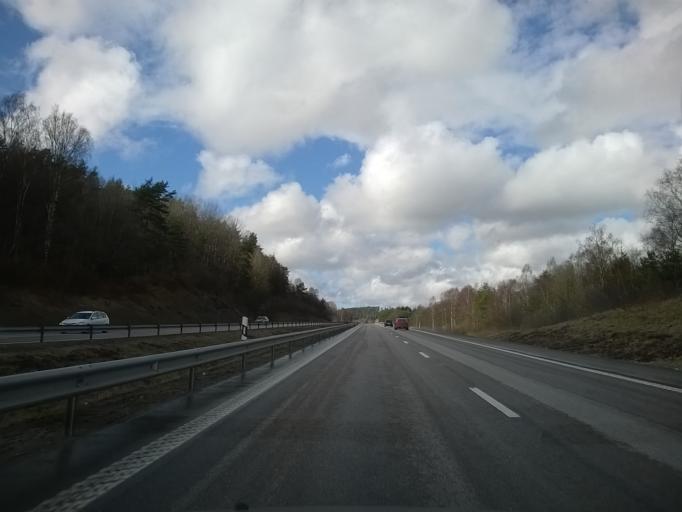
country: SE
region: Halland
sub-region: Kungsbacka Kommun
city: Frillesas
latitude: 57.3762
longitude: 12.1985
